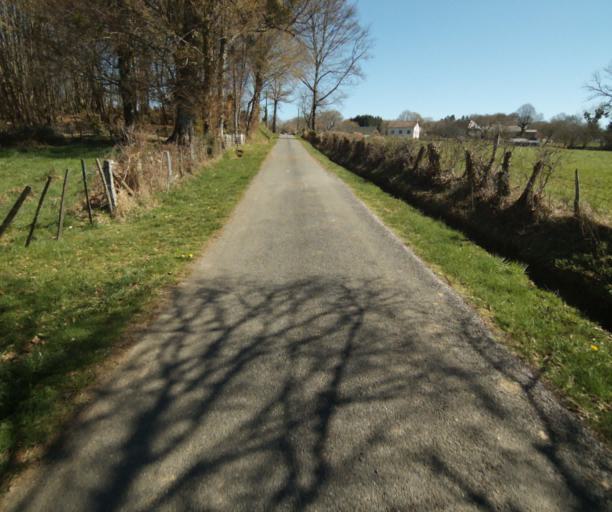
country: FR
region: Limousin
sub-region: Departement de la Correze
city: Uzerche
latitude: 45.4082
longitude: 1.6140
